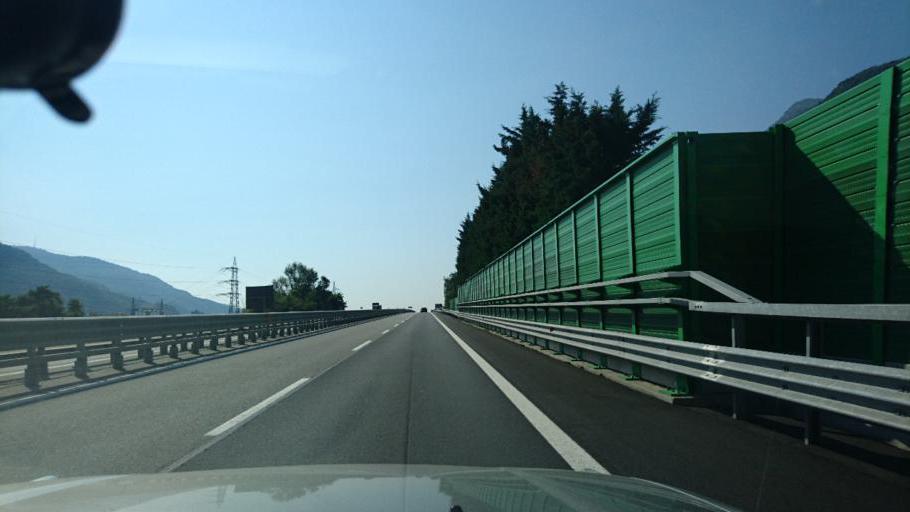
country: IT
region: Piedmont
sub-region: Provincia di Torino
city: Tavagnasco
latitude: 45.5543
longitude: 7.8194
